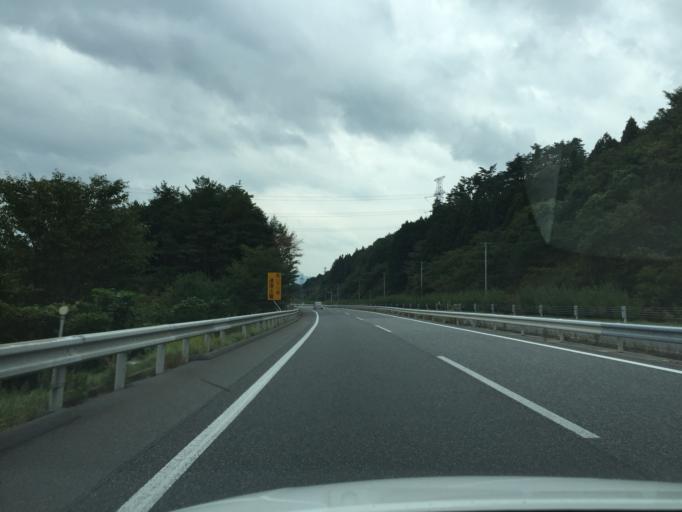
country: JP
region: Fukushima
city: Iwaki
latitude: 37.1665
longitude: 140.7262
